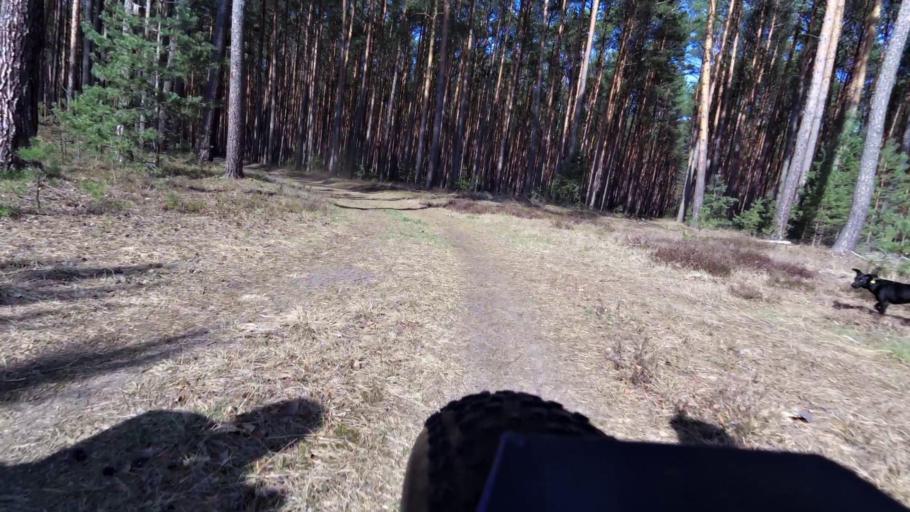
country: PL
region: Lubusz
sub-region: Powiat slubicki
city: Cybinka
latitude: 52.2108
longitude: 14.9088
